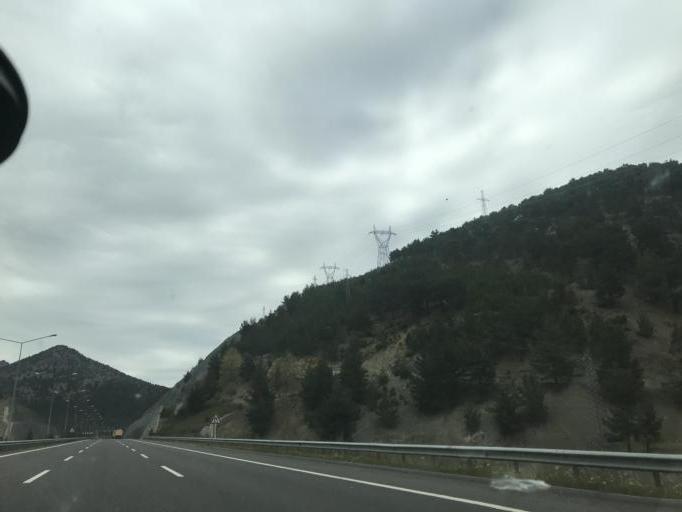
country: TR
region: Nigde
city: Ciftehan
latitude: 37.4986
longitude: 34.8278
